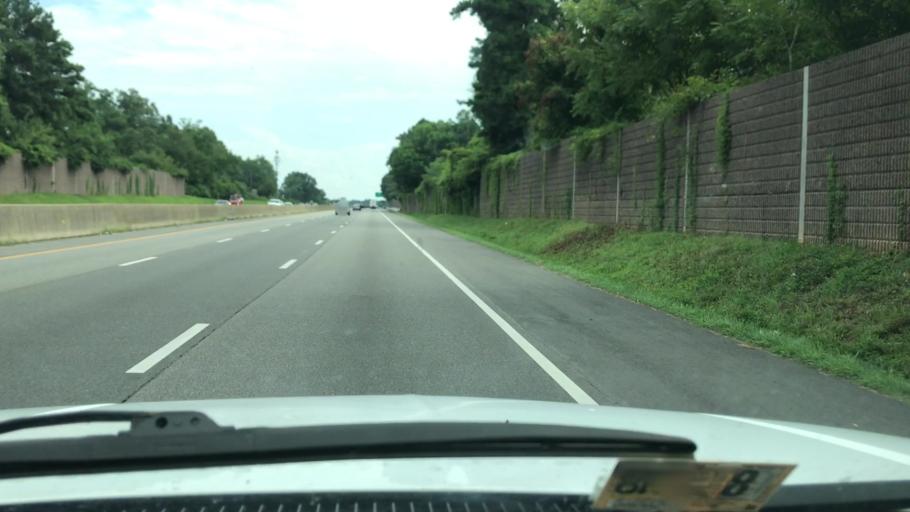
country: US
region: Virginia
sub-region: Chesterfield County
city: Bon Air
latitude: 37.4863
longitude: -77.5187
